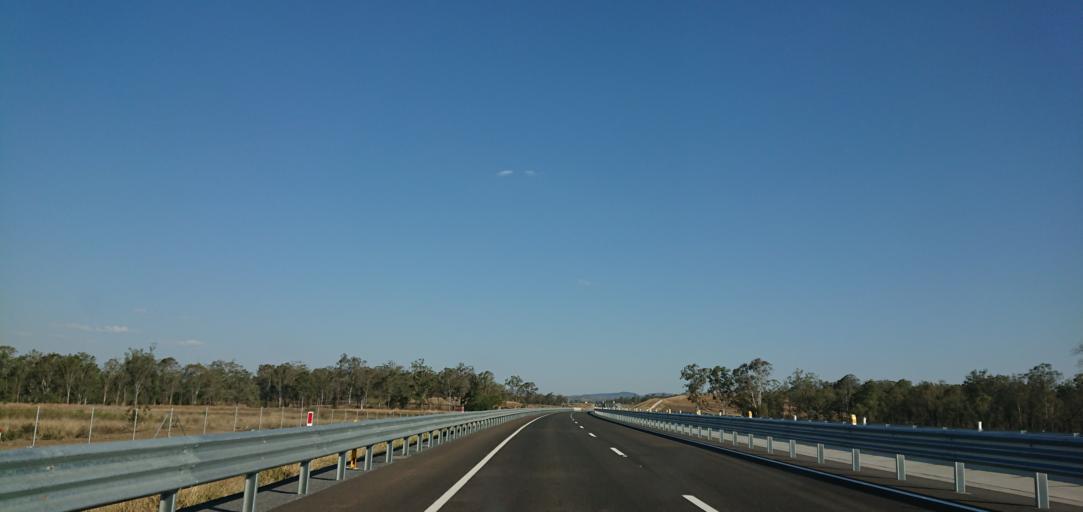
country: AU
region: Queensland
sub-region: Toowoomba
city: Rangeville
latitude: -27.5334
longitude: 152.0751
